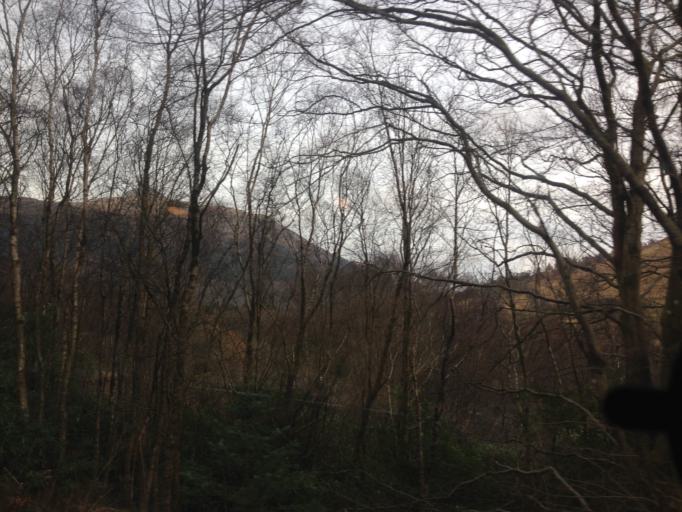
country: GB
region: Scotland
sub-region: Argyll and Bute
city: Garelochhead
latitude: 56.2047
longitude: -4.7191
